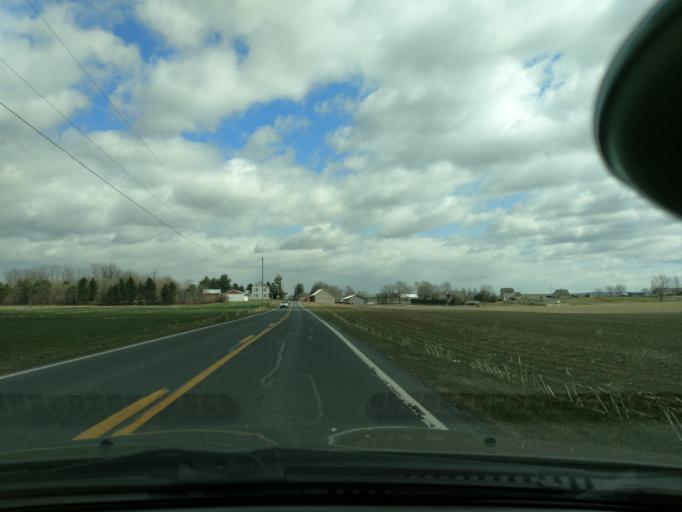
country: US
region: Pennsylvania
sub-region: Lebanon County
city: Avon
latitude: 40.3502
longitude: -76.3594
